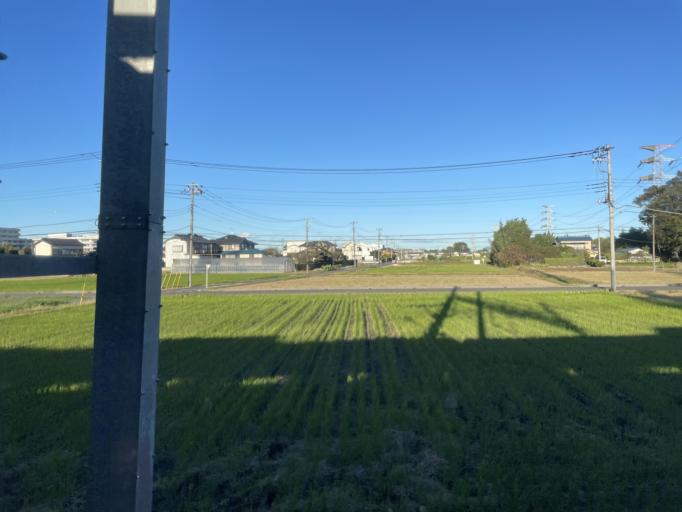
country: JP
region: Saitama
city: Kurihashi
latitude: 36.1110
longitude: 139.7155
